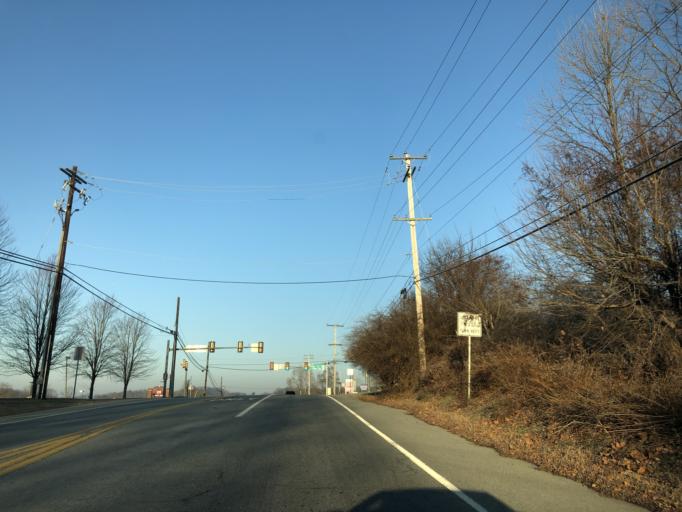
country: US
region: Pennsylvania
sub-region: Chester County
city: West Chester
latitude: 39.9640
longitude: -75.6267
